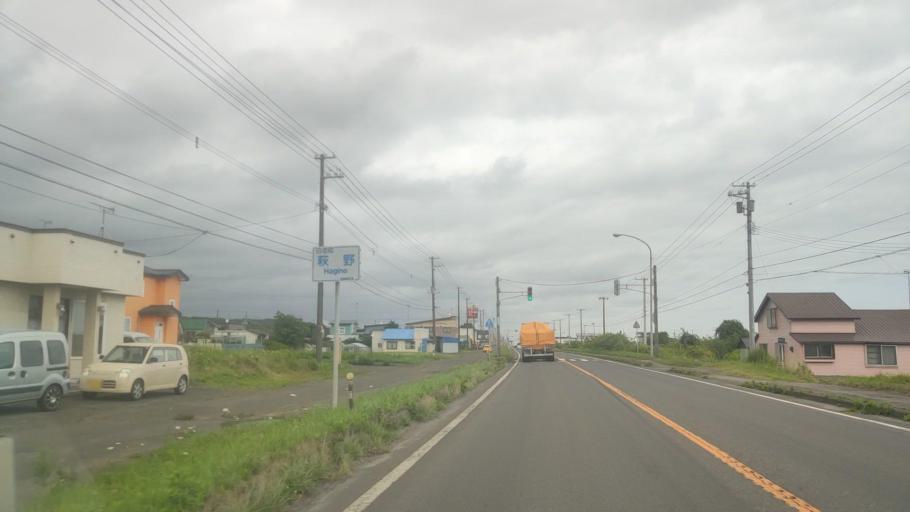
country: JP
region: Hokkaido
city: Shiraoi
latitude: 42.5118
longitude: 141.2932
